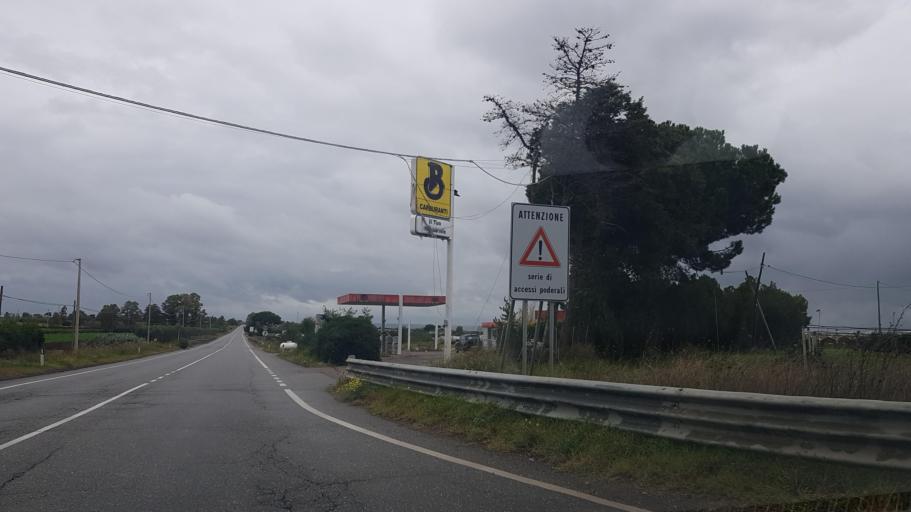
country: IT
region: Apulia
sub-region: Provincia di Taranto
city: Marina di Ginosa
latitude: 40.4047
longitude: 16.8054
